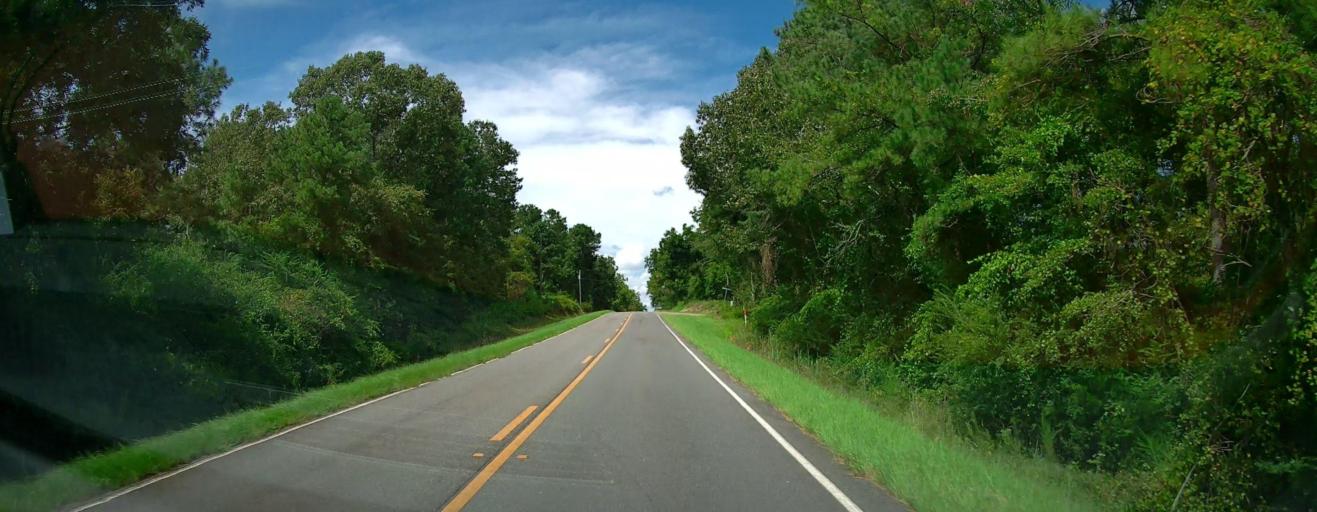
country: US
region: Georgia
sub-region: Taylor County
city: Butler
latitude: 32.4851
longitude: -84.2057
